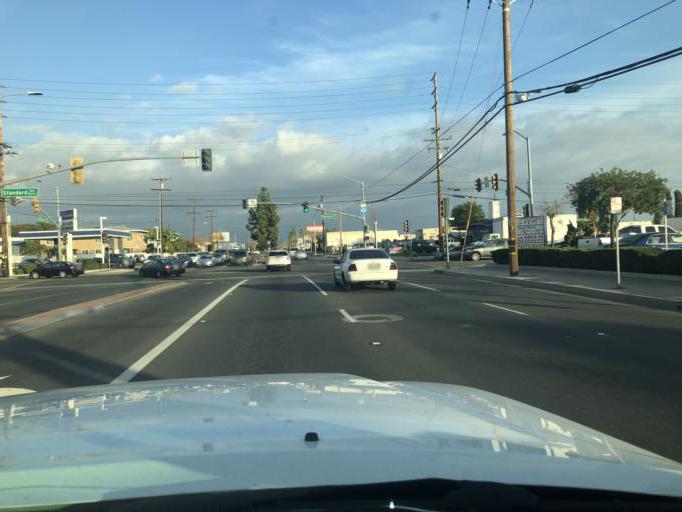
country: US
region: California
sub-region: Orange County
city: Santa Ana
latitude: 33.7268
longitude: -117.8570
